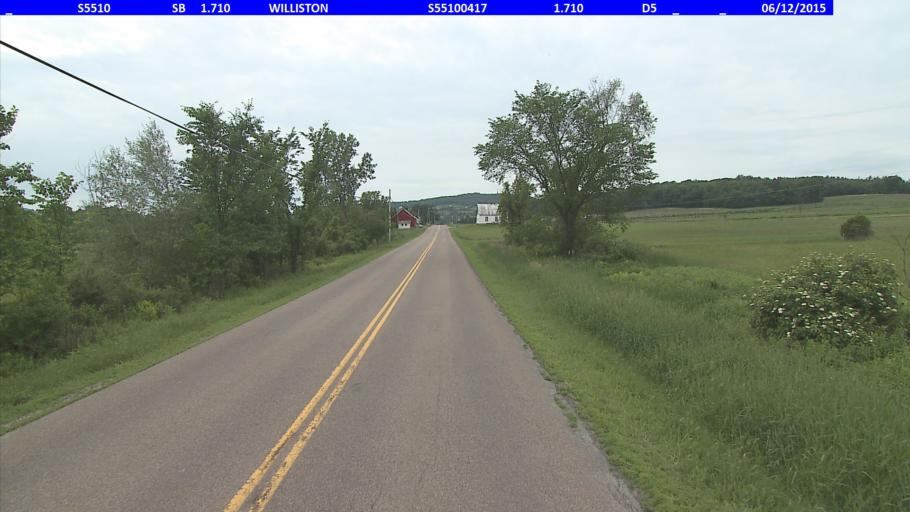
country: US
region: Vermont
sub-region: Chittenden County
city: Williston
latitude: 44.3967
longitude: -73.0930
